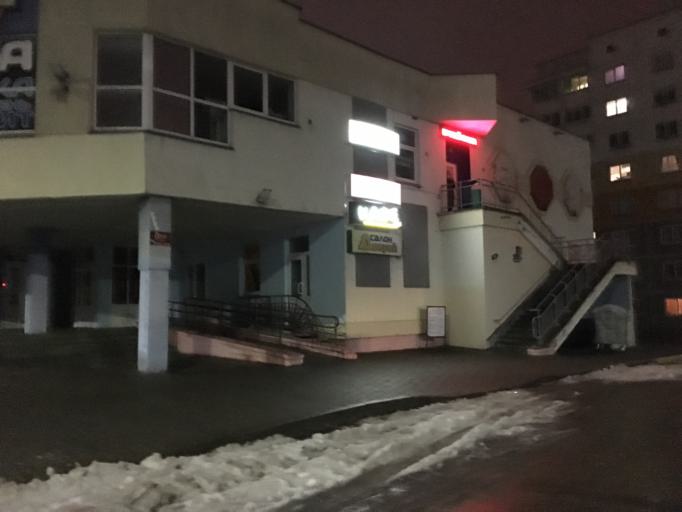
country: BY
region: Grodnenskaya
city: Hrodna
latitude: 53.6954
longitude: 23.8349
